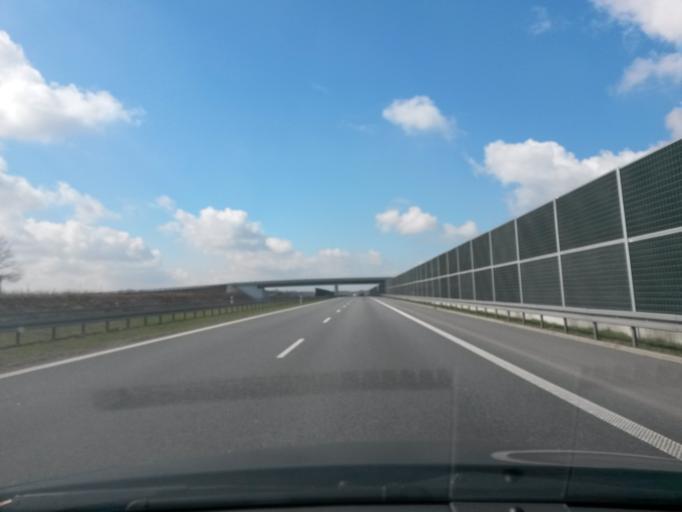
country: PL
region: Masovian Voivodeship
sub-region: Powiat zyrardowski
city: Guzow
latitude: 52.0744
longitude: 20.2618
